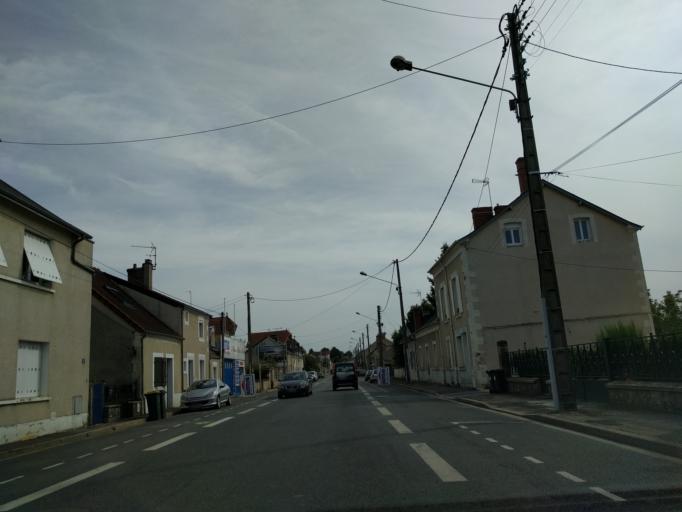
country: FR
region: Centre
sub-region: Departement du Cher
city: Bourges
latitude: 47.0663
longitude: 2.4180
